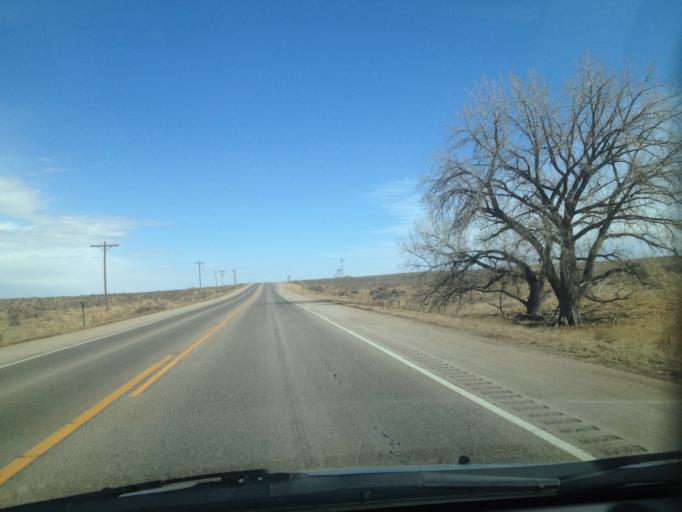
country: US
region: Colorado
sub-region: Weld County
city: Kersey
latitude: 40.2937
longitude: -104.2961
